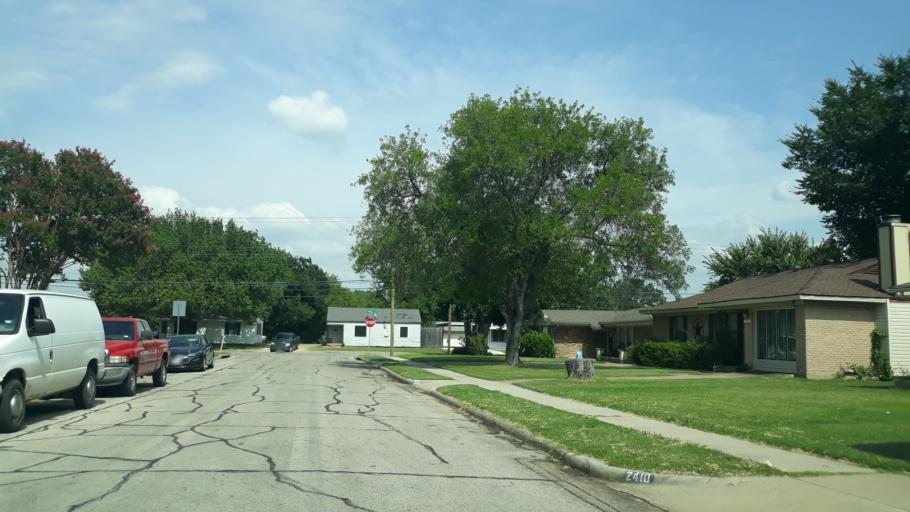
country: US
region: Texas
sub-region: Dallas County
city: Irving
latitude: 32.8128
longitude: -96.9773
